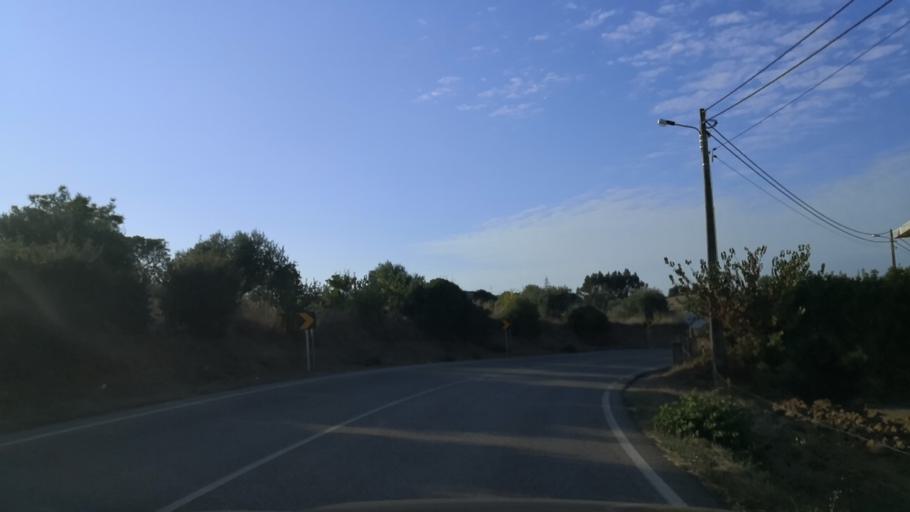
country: PT
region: Santarem
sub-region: Alcanena
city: Alcanena
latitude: 39.3497
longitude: -8.6653
